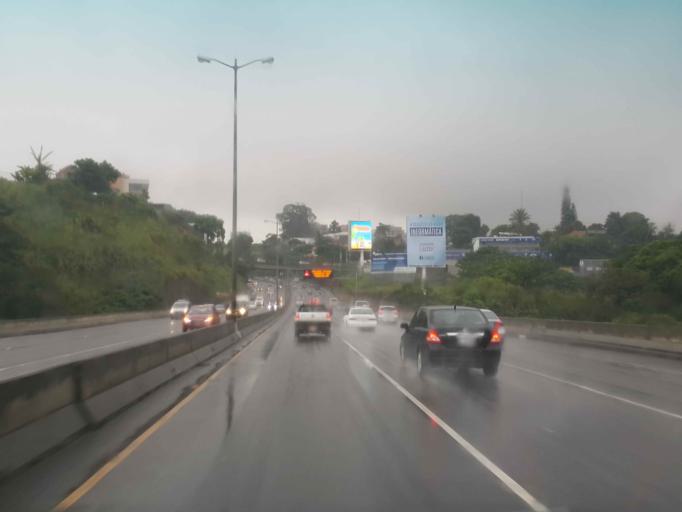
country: CR
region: San Jose
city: San Rafael
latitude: 9.9355
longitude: -84.1234
